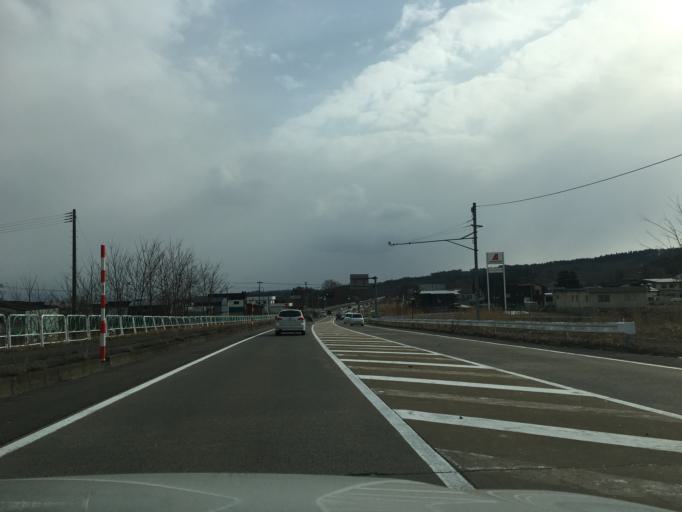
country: JP
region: Aomori
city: Namioka
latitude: 40.7586
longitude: 140.5867
